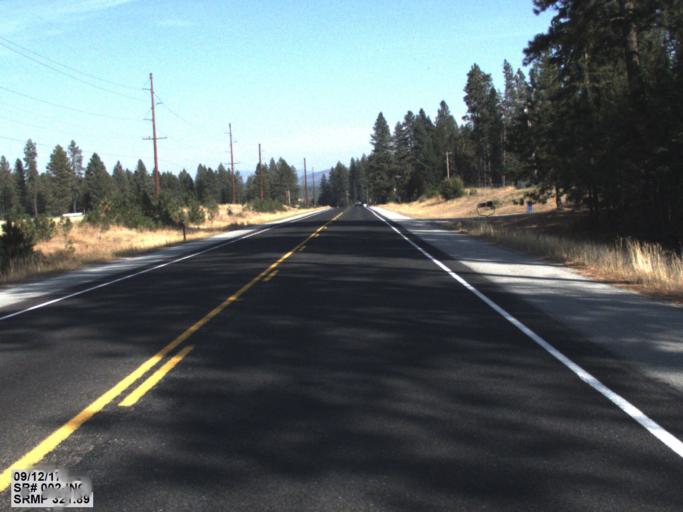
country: US
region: Washington
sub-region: Pend Oreille County
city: Newport
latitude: 48.0973
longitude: -117.2678
